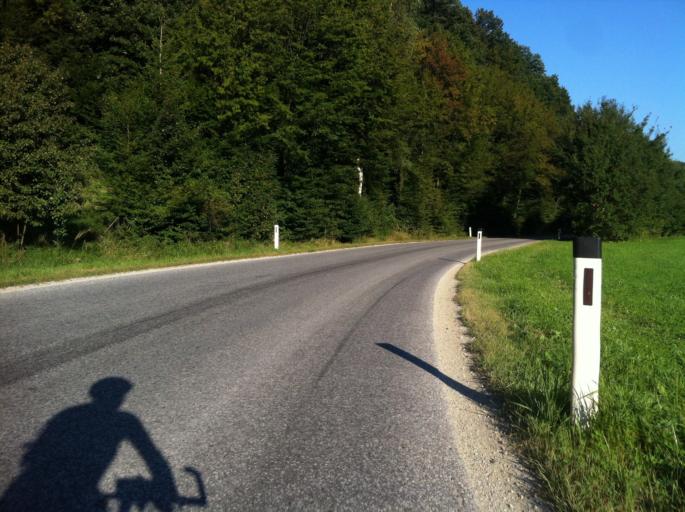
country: AT
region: Lower Austria
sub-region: Politischer Bezirk Wien-Umgebung
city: Pressbaum
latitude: 48.2009
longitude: 16.1108
